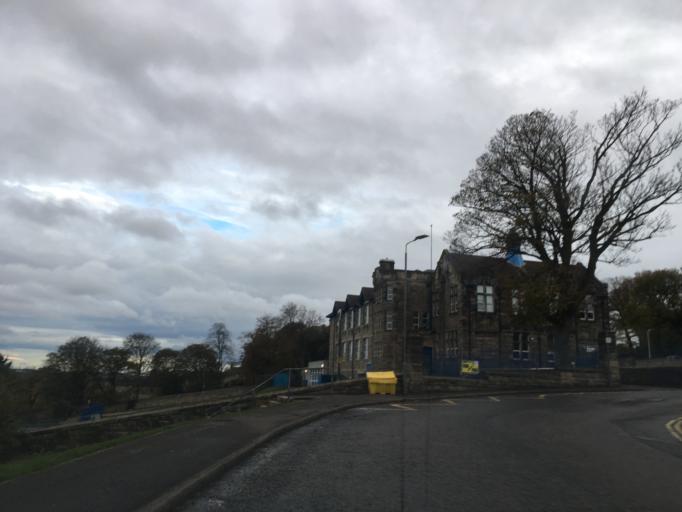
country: GB
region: Scotland
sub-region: Falkirk
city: Bo'ness
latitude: 56.0147
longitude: -3.5915
